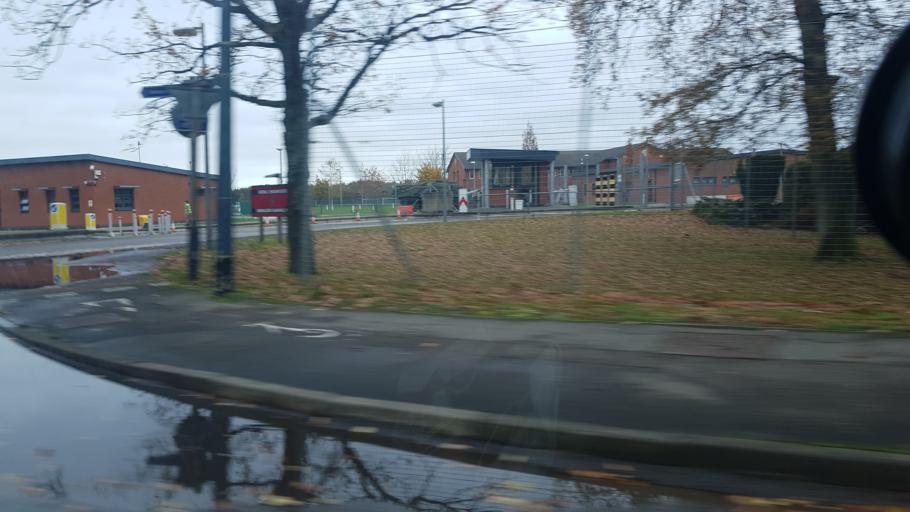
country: GB
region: England
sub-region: Hampshire
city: Yateley
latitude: 51.3181
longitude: -0.8212
